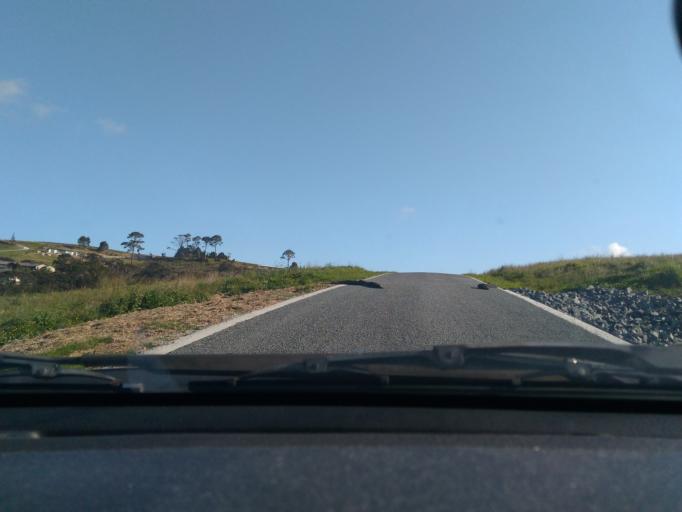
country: NZ
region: Auckland
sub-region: Auckland
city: Warkworth
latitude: -36.4408
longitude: 174.7524
